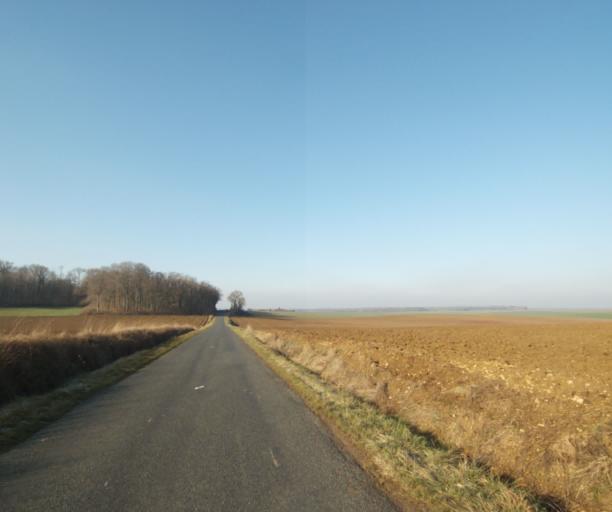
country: FR
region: Champagne-Ardenne
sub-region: Departement de la Haute-Marne
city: Chevillon
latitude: 48.4873
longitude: 5.0816
